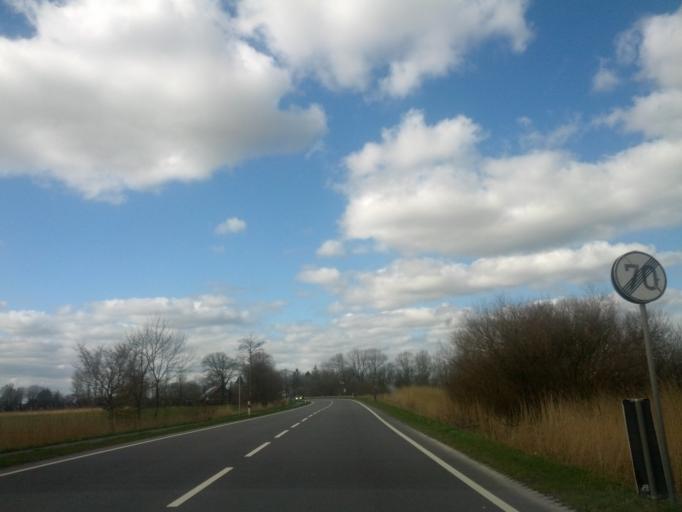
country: DE
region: Lower Saxony
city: Jever
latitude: 53.5789
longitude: 7.8473
